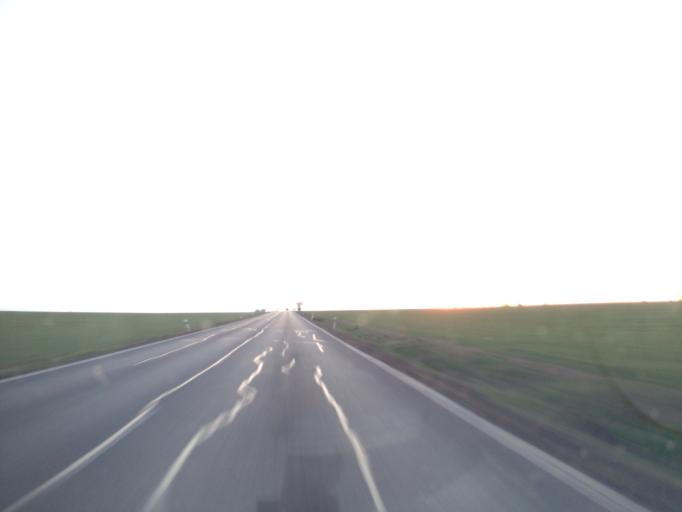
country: CZ
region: Central Bohemia
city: Rakovnik
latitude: 50.1666
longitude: 13.6346
